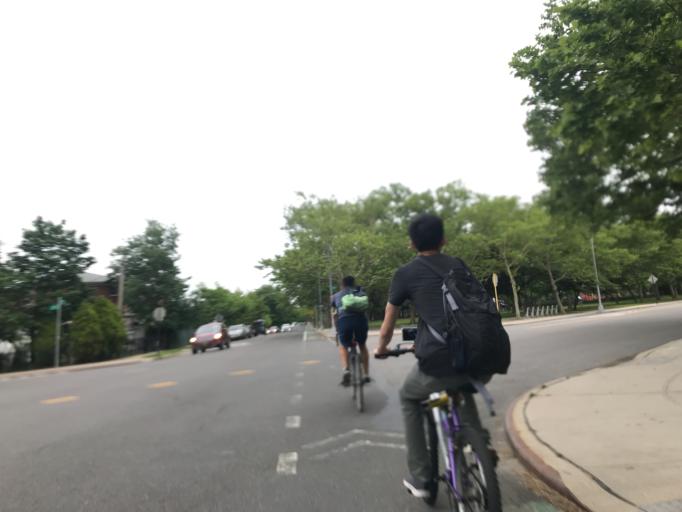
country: US
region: New York
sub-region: Queens County
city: Jamaica
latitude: 40.7459
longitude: -73.7896
